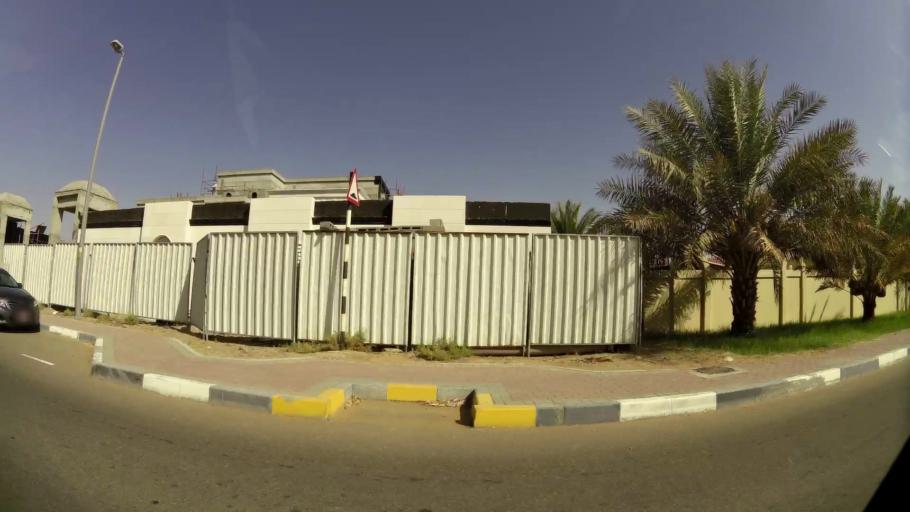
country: OM
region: Al Buraimi
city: Al Buraymi
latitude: 24.3315
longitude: 55.7958
